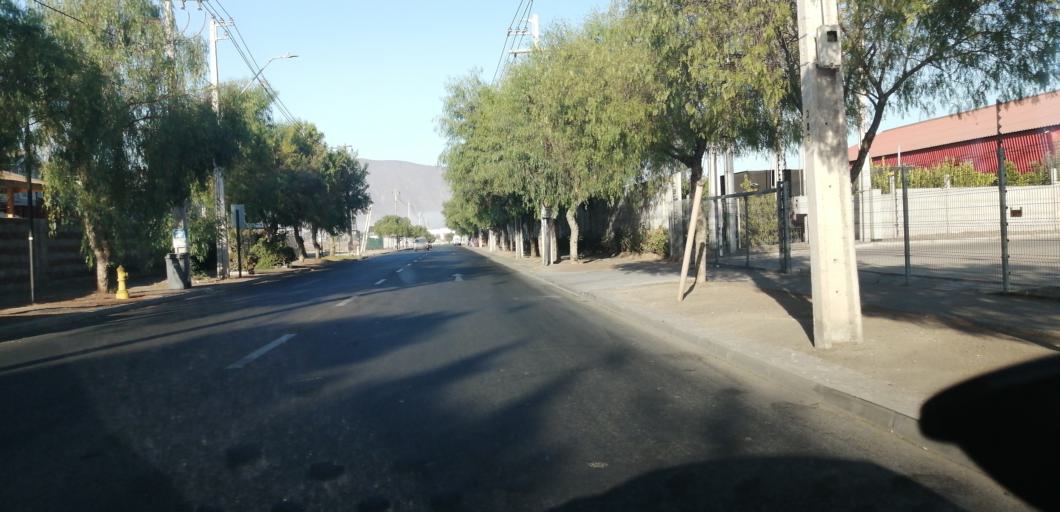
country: CL
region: Santiago Metropolitan
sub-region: Provincia de Santiago
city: Lo Prado
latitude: -33.4339
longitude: -70.7810
